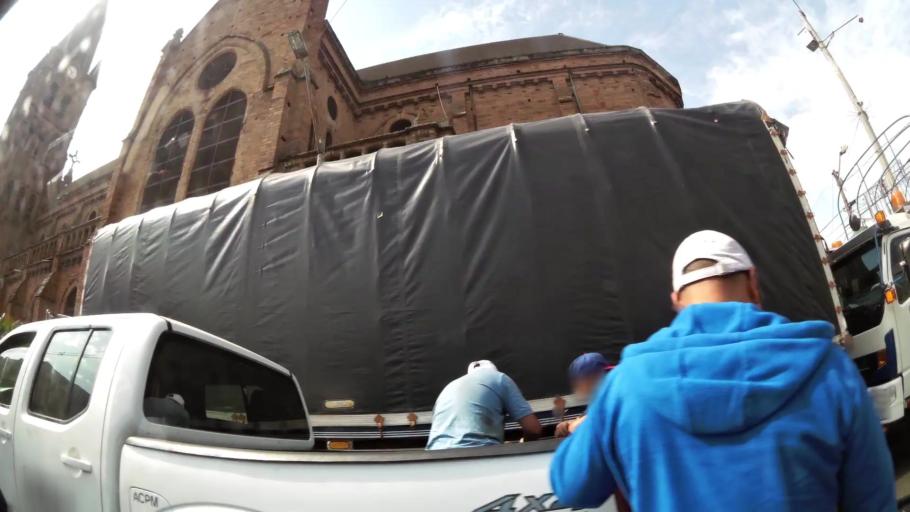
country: CO
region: Antioquia
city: Medellin
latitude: 6.2480
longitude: -75.5764
